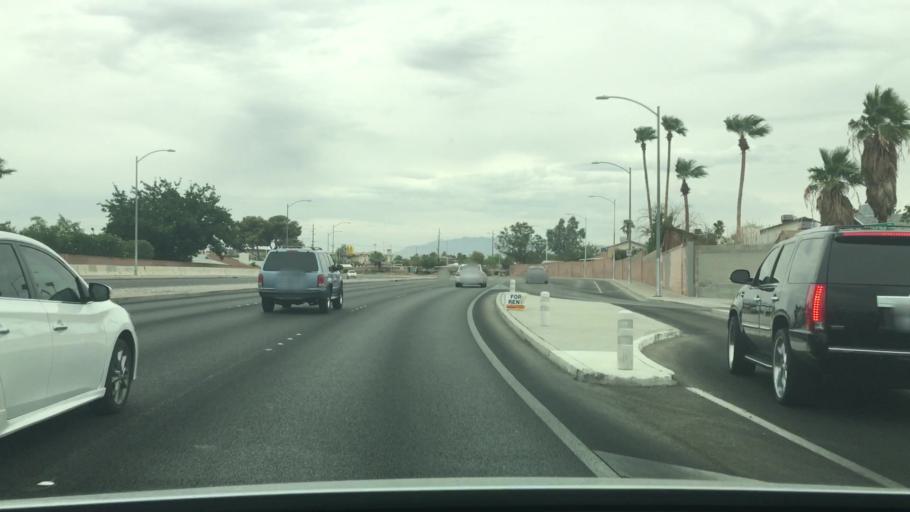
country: US
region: Nevada
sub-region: Clark County
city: Spring Valley
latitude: 36.1620
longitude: -115.2607
